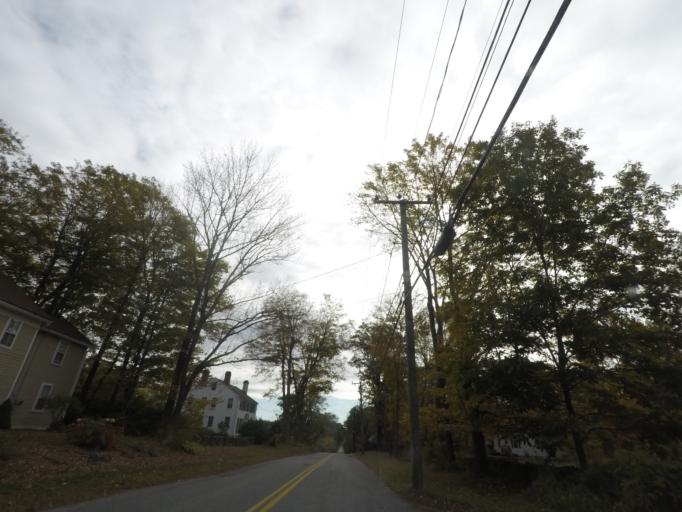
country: US
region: Connecticut
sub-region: Windham County
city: Thompson
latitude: 41.9575
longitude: -71.8601
